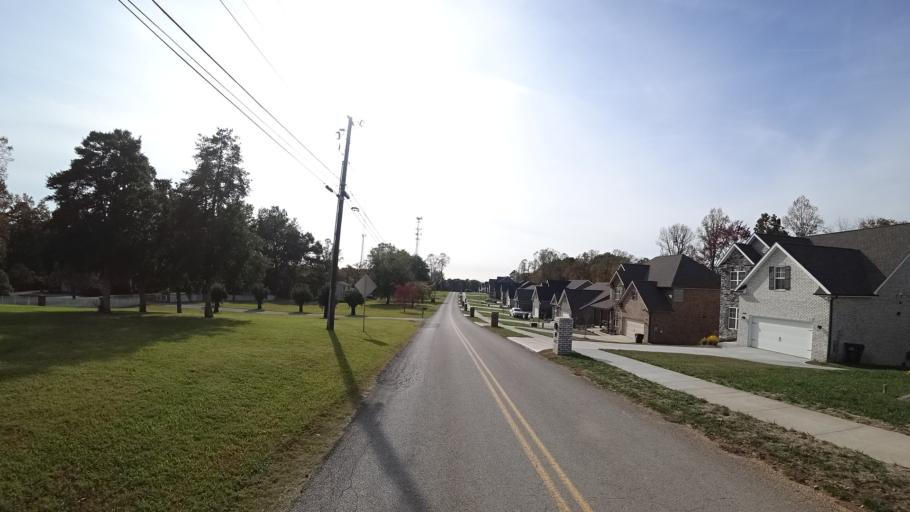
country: US
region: Tennessee
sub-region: Knox County
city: Farragut
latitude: 35.9064
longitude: -84.1850
